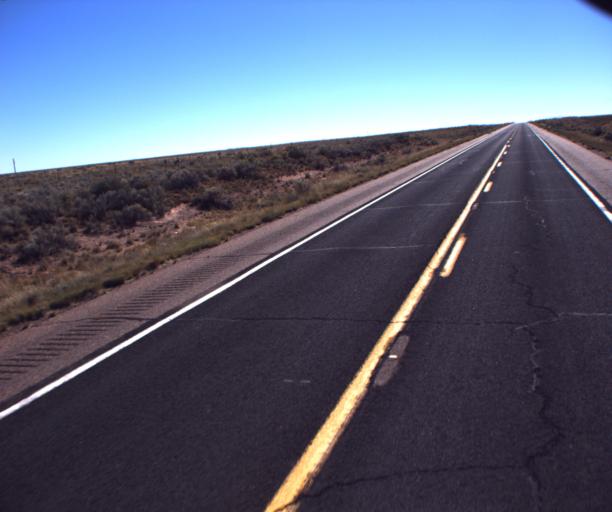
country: US
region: Arizona
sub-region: Navajo County
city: Snowflake
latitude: 34.7116
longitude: -109.7639
